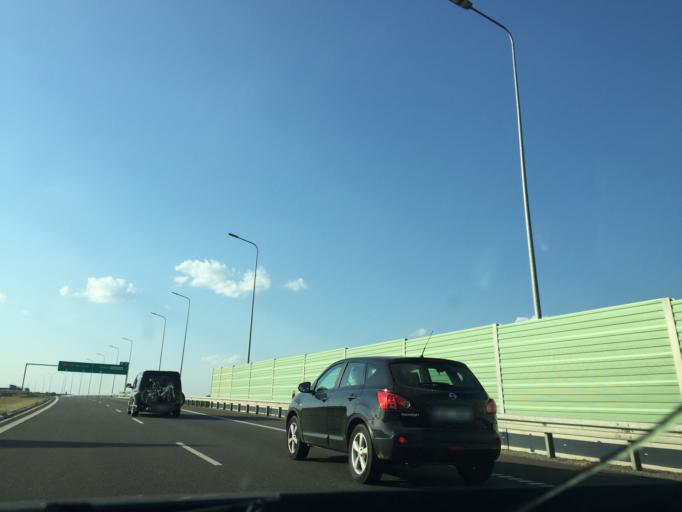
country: PL
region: Masovian Voivodeship
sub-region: Powiat radomski
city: Jedlinsk
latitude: 51.5295
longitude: 21.0816
